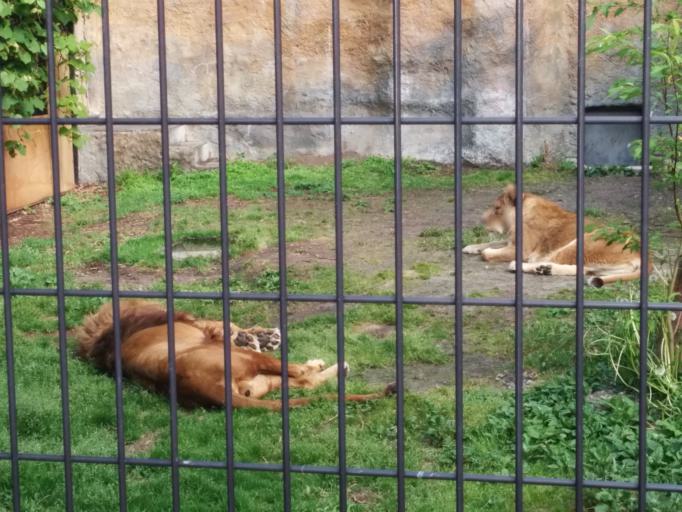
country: JP
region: Hokkaido
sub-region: Asahikawa-shi
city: Asahikawa
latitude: 43.7678
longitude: 142.4785
